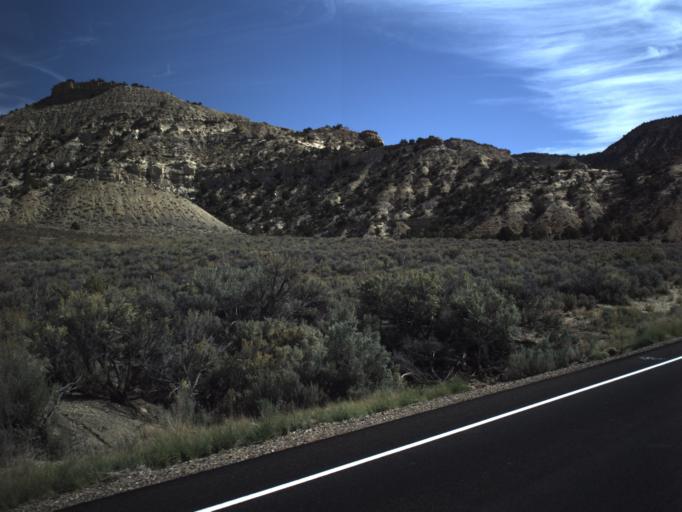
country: US
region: Utah
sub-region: Garfield County
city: Panguitch
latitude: 37.5931
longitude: -111.9357
